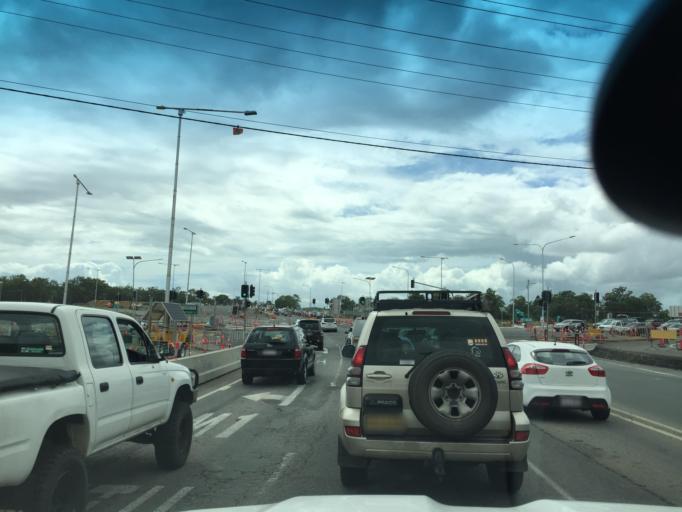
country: AU
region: Queensland
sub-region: Moreton Bay
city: Burpengary
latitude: -27.1792
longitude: 152.9806
